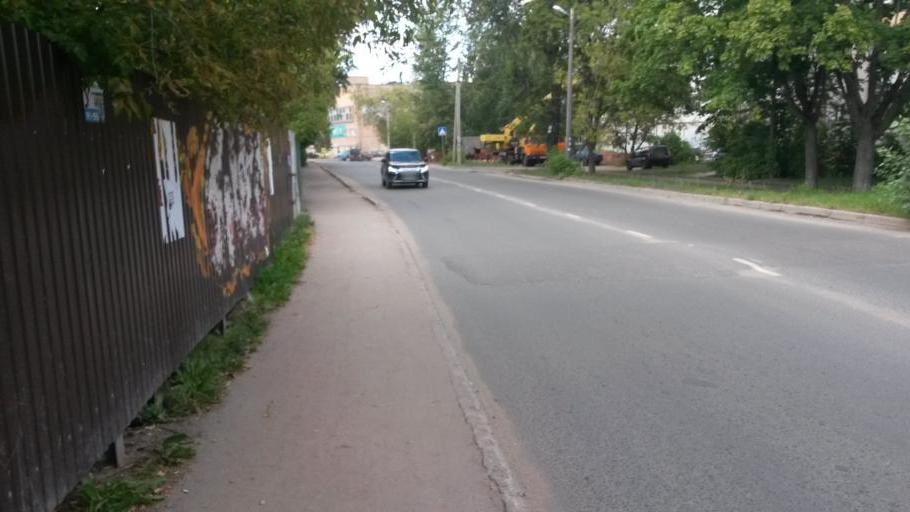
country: RU
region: Ivanovo
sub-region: Gorod Ivanovo
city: Ivanovo
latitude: 57.0076
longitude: 40.9587
